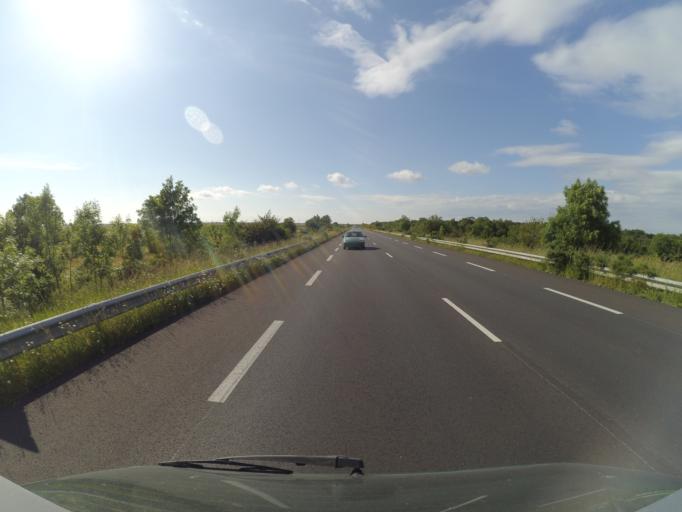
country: FR
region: Poitou-Charentes
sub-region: Departement de la Charente-Maritime
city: Saint-Agnant
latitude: 45.8433
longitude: -0.9494
